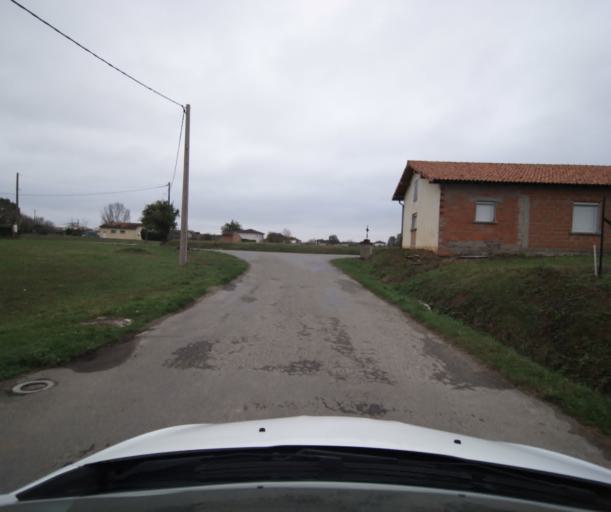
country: FR
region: Midi-Pyrenees
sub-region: Departement du Tarn-et-Garonne
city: Moissac
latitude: 44.0716
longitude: 1.1285
